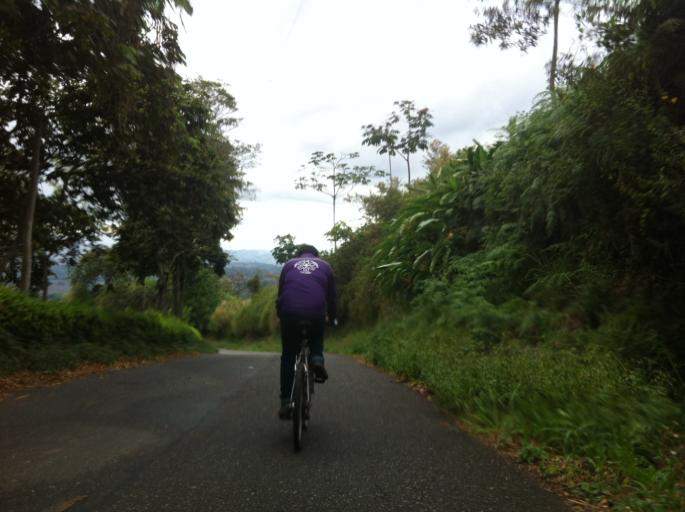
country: CO
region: Quindio
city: Buenavista
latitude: 4.3688
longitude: -75.7525
